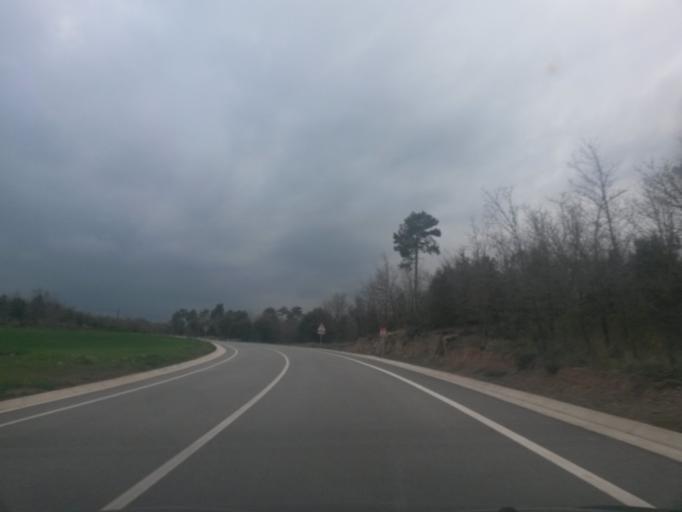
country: ES
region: Catalonia
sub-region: Provincia de Barcelona
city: Sagas
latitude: 42.0324
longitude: 1.9853
